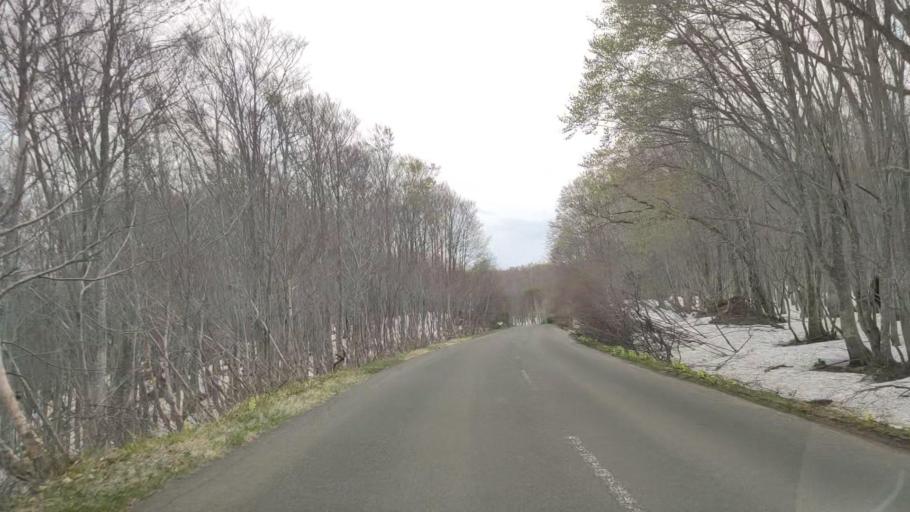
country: JP
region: Aomori
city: Aomori Shi
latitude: 40.6894
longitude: 140.9171
